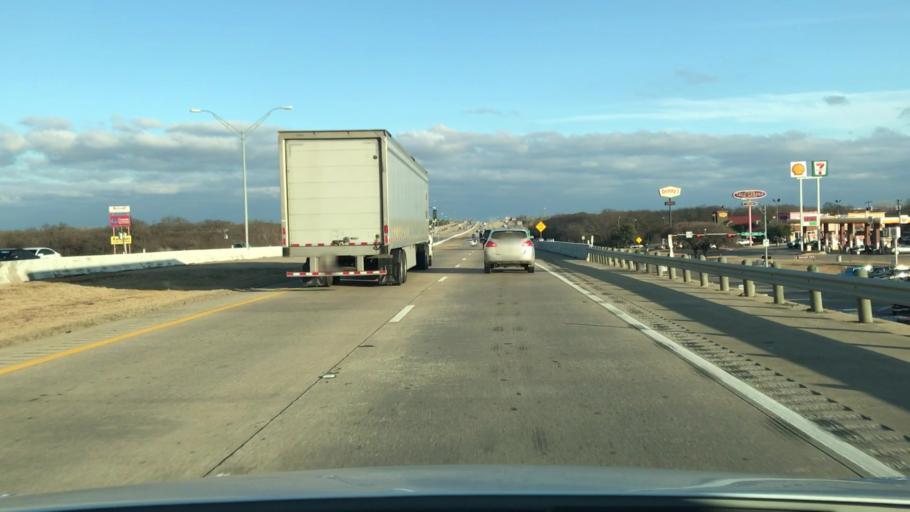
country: US
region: Texas
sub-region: Dallas County
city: Mesquite
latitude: 32.7905
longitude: -96.5967
